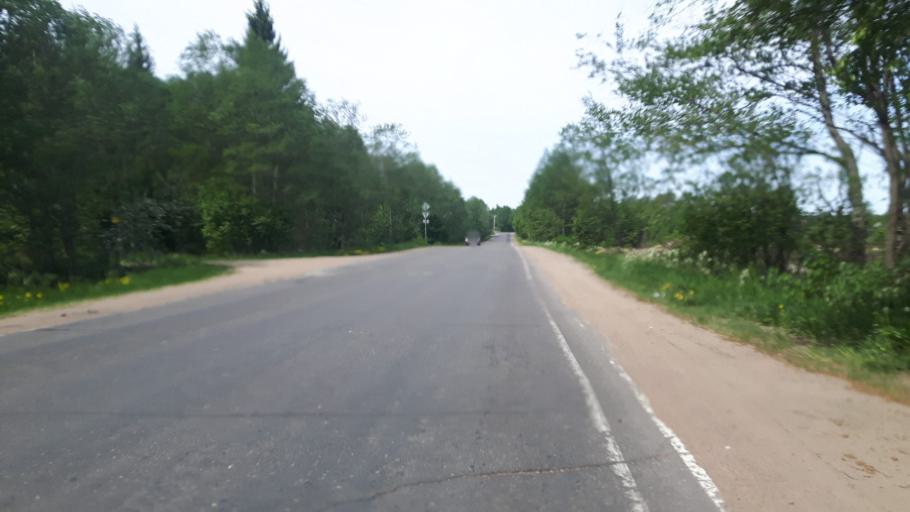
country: RU
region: Leningrad
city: Ust'-Luga
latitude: 59.6378
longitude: 28.2854
